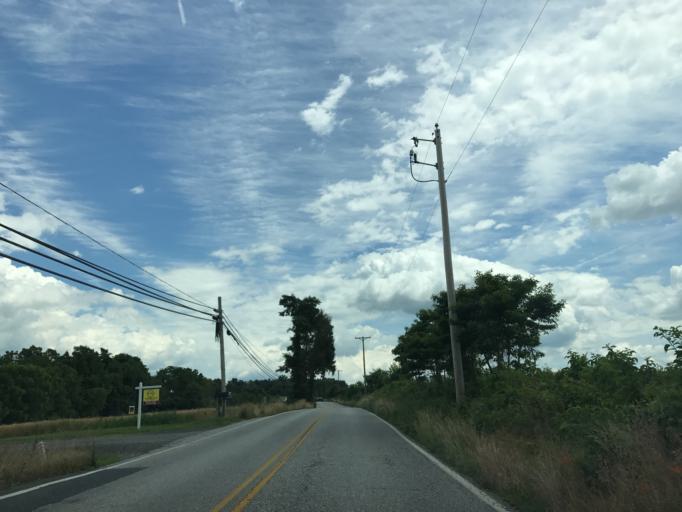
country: US
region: Maryland
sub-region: Harford County
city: Jarrettsville
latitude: 39.5996
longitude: -76.5000
